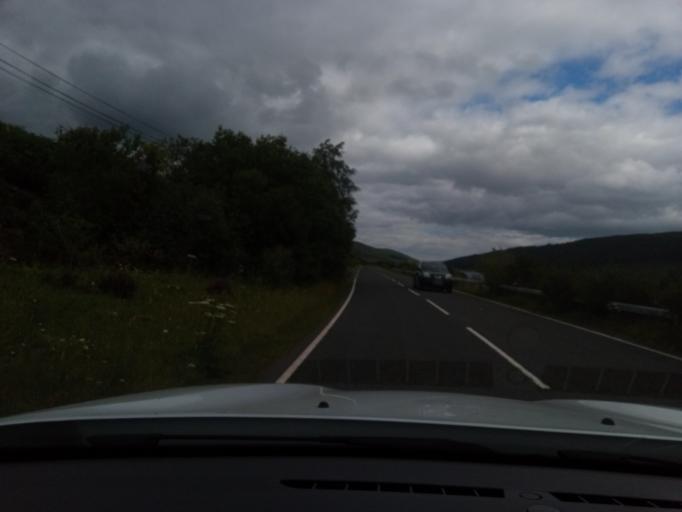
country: GB
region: Scotland
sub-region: The Scottish Borders
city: Peebles
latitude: 55.4972
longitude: -3.1860
